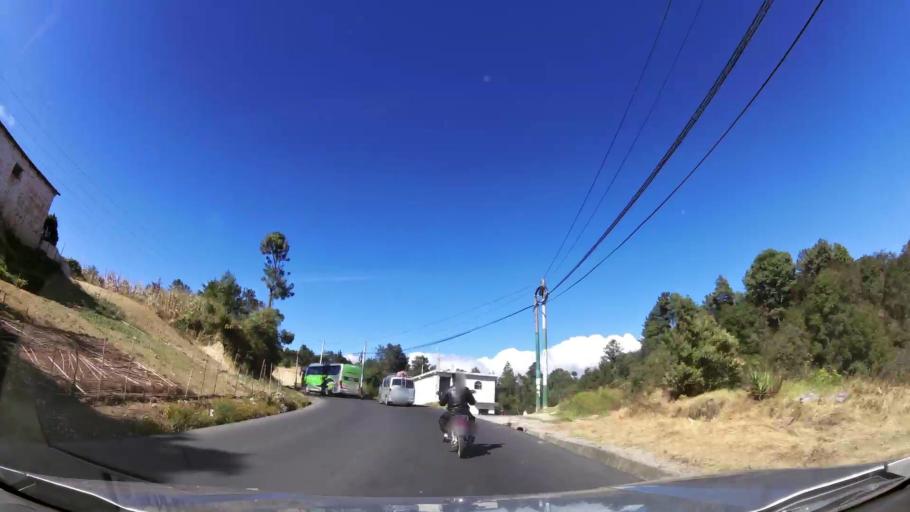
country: GT
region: Solola
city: Solola
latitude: 14.7839
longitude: -91.1819
